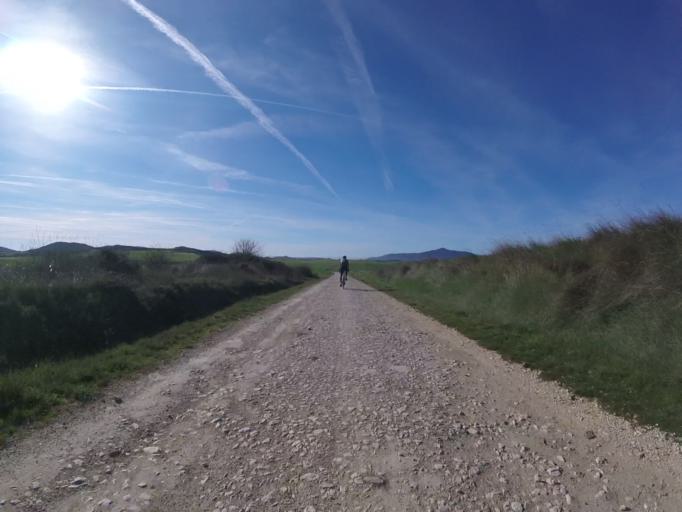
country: ES
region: Navarre
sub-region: Provincia de Navarra
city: Yerri
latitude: 42.7164
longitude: -1.9701
